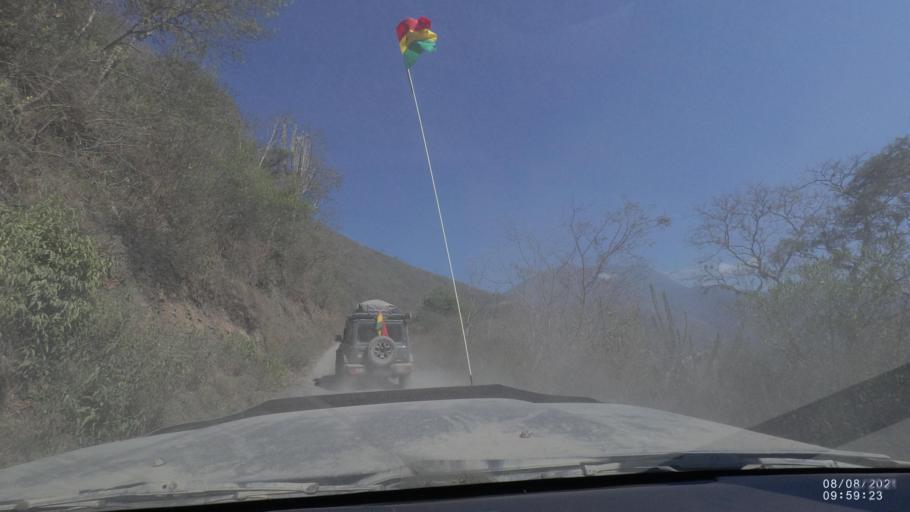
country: BO
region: La Paz
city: Quime
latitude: -16.6459
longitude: -66.7232
